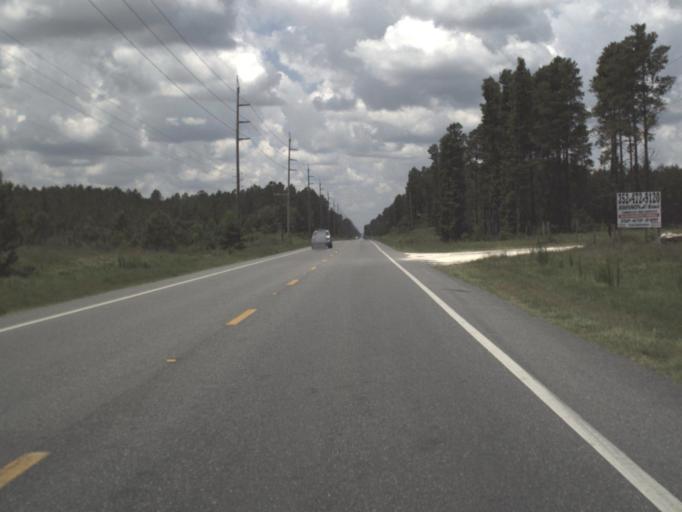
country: US
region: Florida
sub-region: Alachua County
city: Newberry
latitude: 29.6306
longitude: -82.7084
